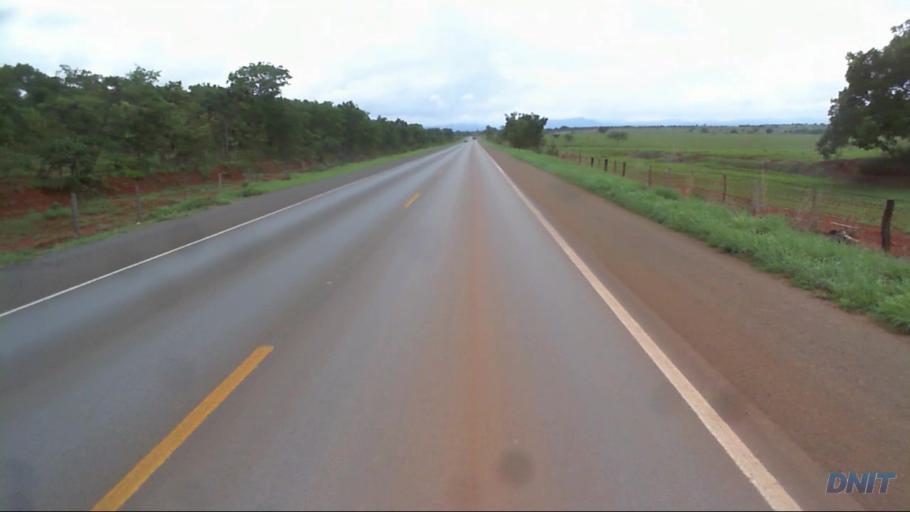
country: BR
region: Goias
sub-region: Padre Bernardo
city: Padre Bernardo
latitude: -15.1649
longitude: -48.3624
